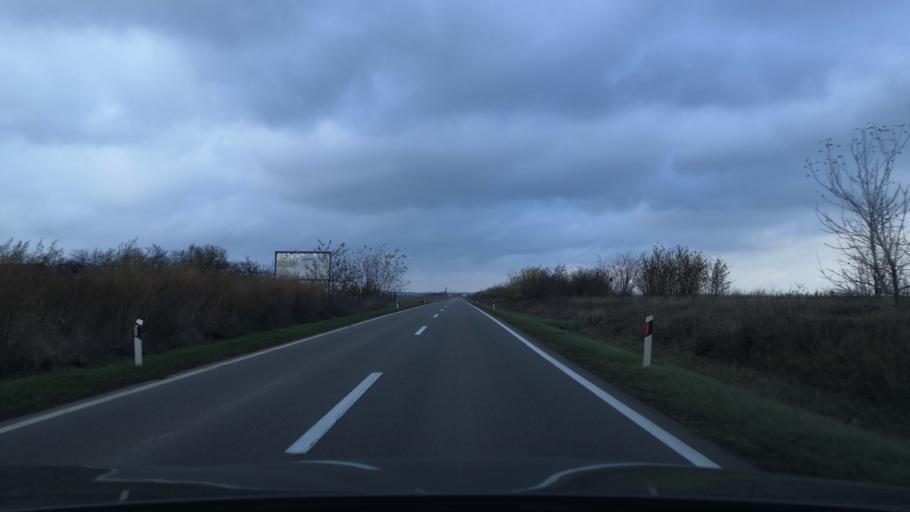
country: RS
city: Sanad
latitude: 45.9937
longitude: 20.1064
